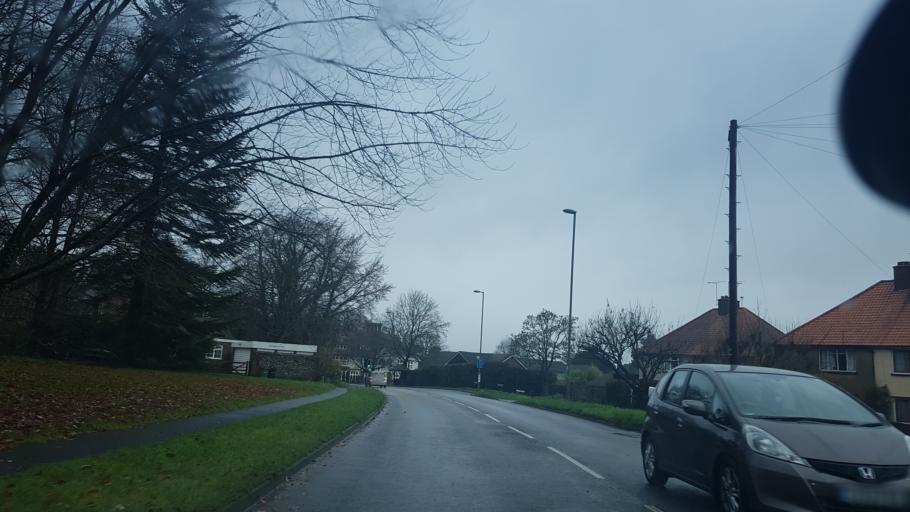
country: GB
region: England
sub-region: Surrey
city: Great Bookham
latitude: 51.2777
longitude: -0.3707
